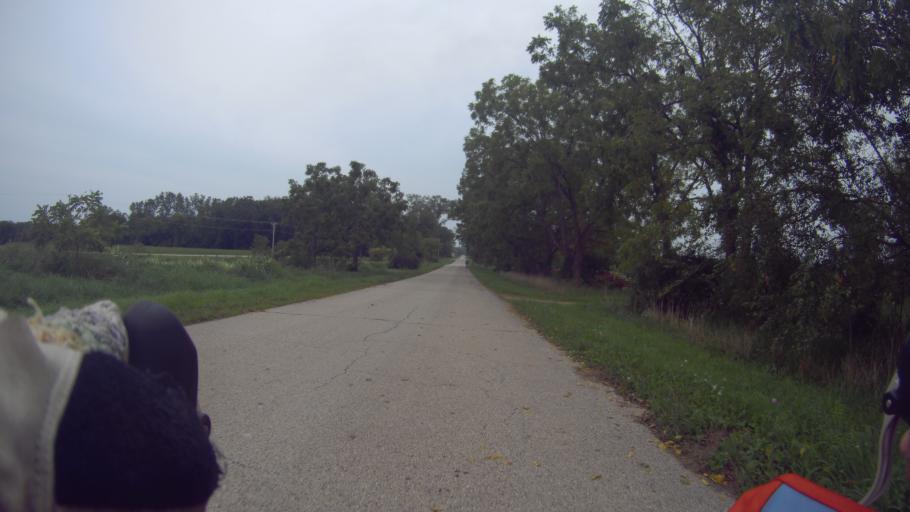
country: US
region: Wisconsin
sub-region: Dane County
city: Verona
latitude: 42.9295
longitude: -89.5369
